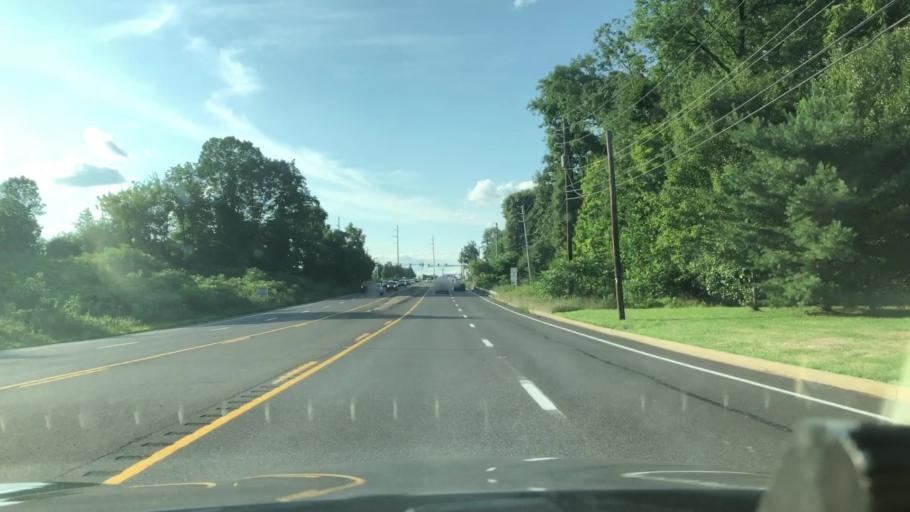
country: US
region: Pennsylvania
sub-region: Bucks County
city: Quakertown
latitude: 40.4568
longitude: -75.3663
